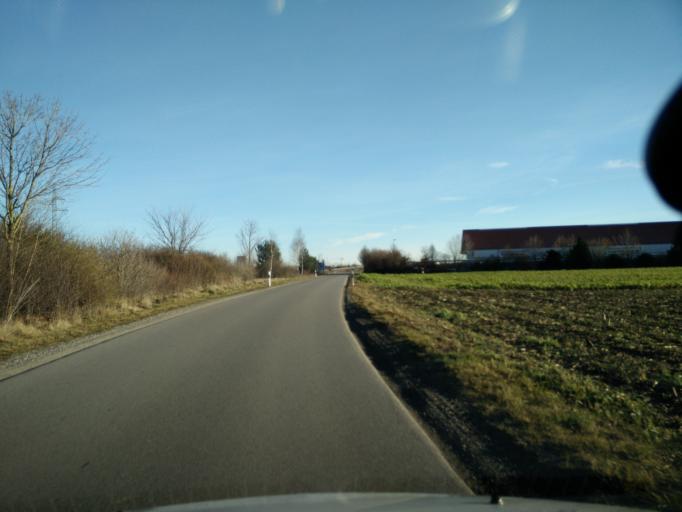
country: DE
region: Bavaria
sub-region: Upper Bavaria
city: Germering
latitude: 48.1446
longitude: 11.3863
